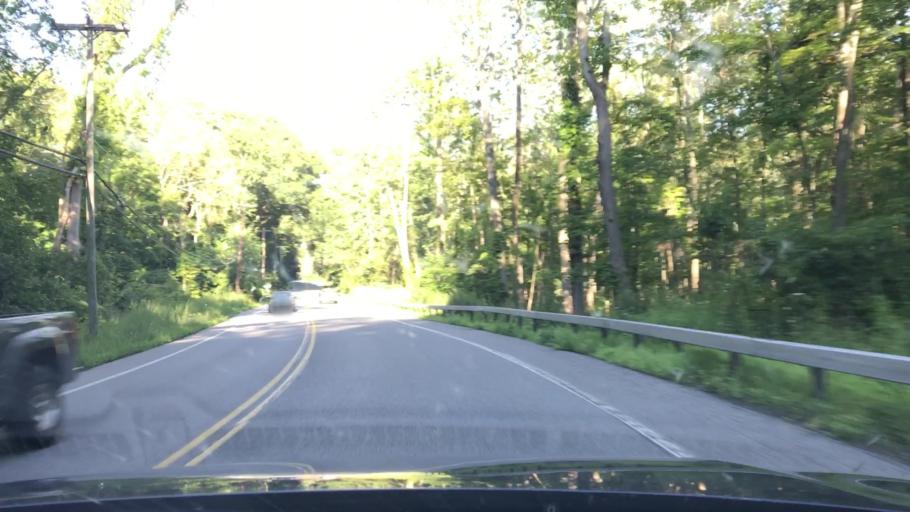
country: US
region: New York
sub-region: Westchester County
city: Heritage Hills
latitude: 41.3686
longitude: -73.6952
